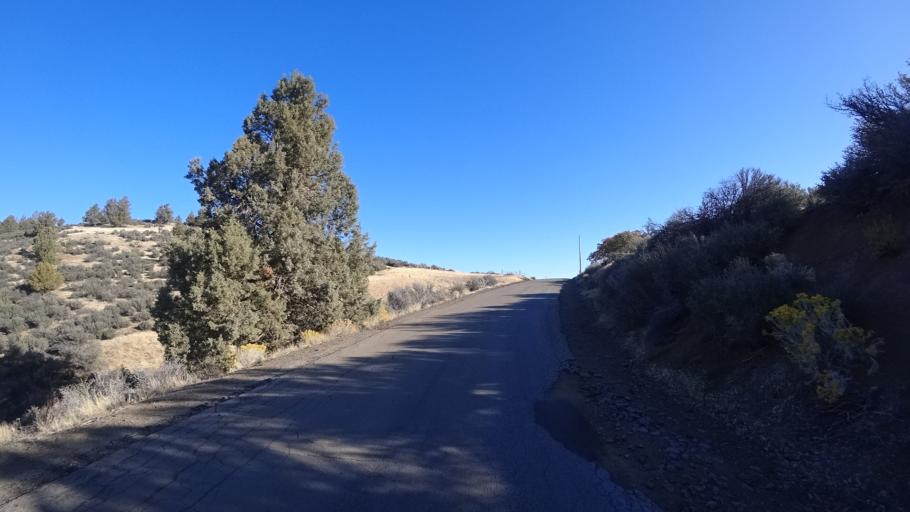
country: US
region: California
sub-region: Siskiyou County
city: Montague
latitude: 41.8789
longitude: -122.4591
